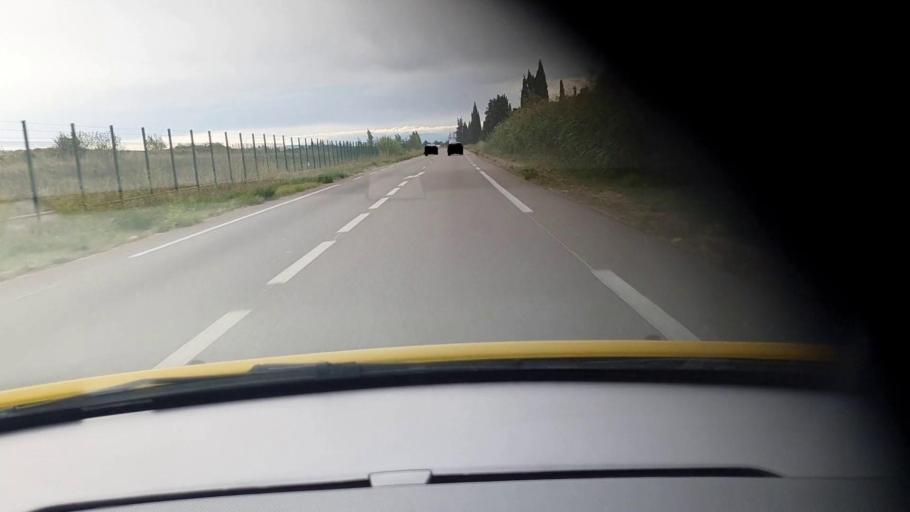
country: FR
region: Languedoc-Roussillon
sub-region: Departement du Gard
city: Garons
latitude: 43.7454
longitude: 4.4089
